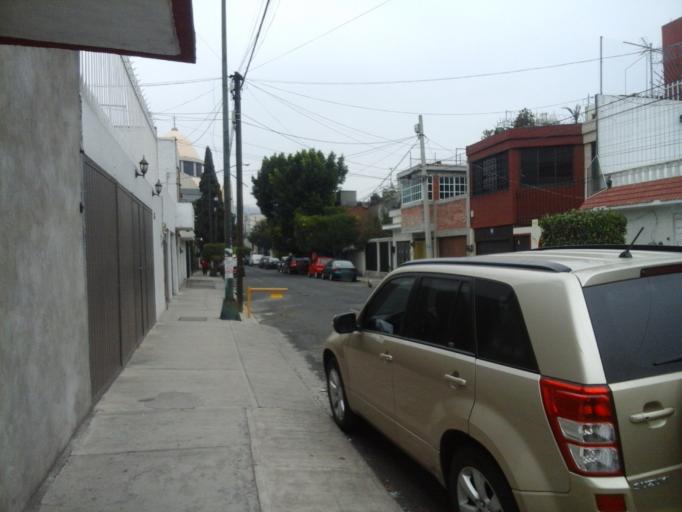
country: MX
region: Mexico
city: Colonia Lindavista
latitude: 19.4889
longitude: -99.1333
